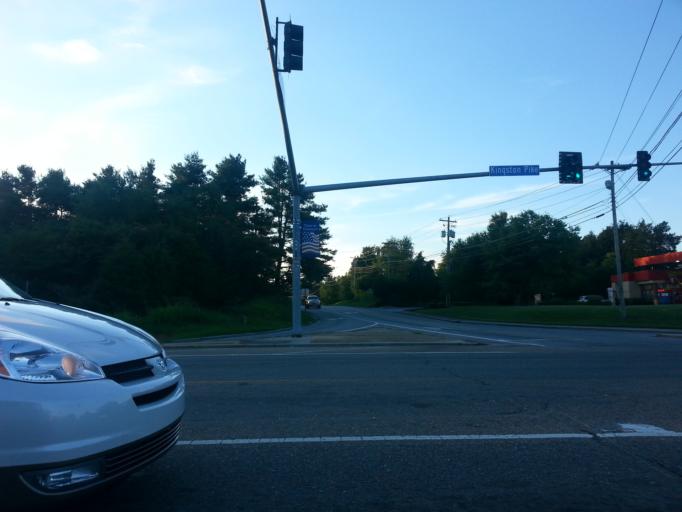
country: US
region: Tennessee
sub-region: Knox County
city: Farragut
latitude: 35.8622
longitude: -84.2213
